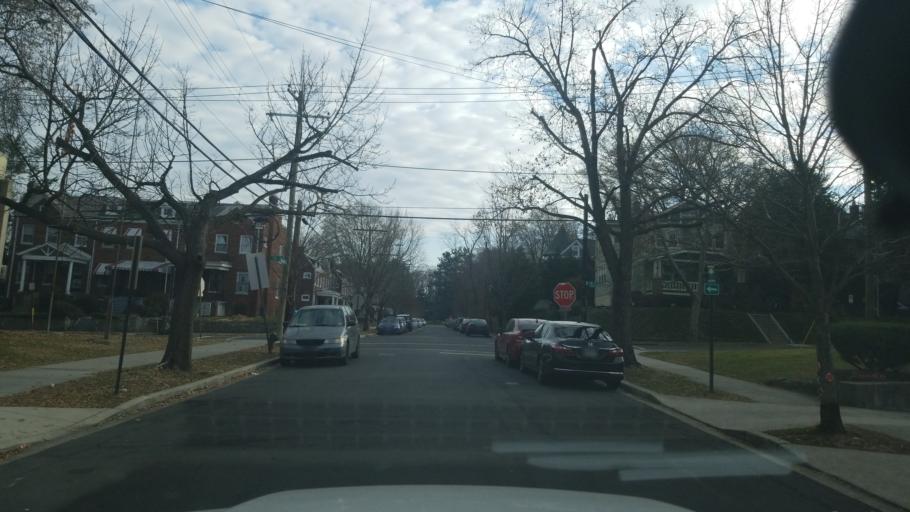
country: US
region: Maryland
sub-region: Prince George's County
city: Mount Rainier
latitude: 38.9383
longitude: -76.9888
